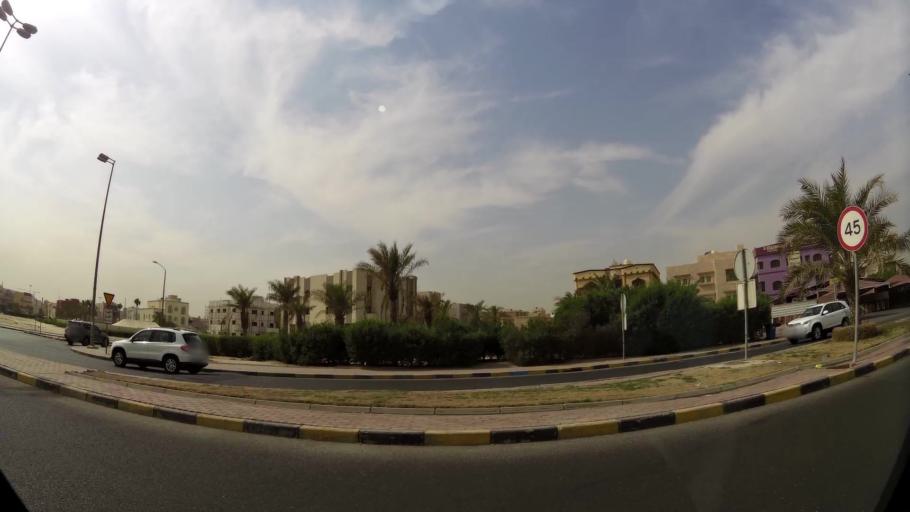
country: KW
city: Bayan
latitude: 29.2904
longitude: 48.0177
